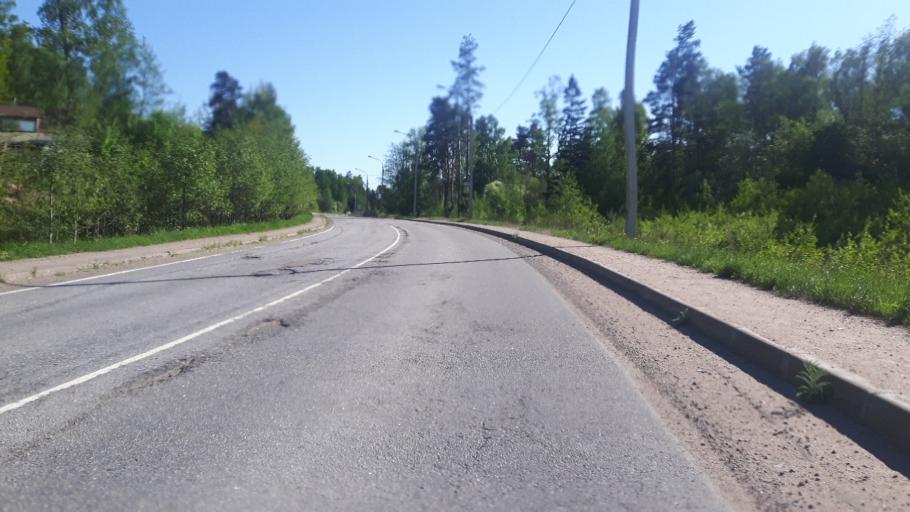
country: RU
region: Leningrad
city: Sosnovyy Bor
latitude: 60.2117
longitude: 29.0063
